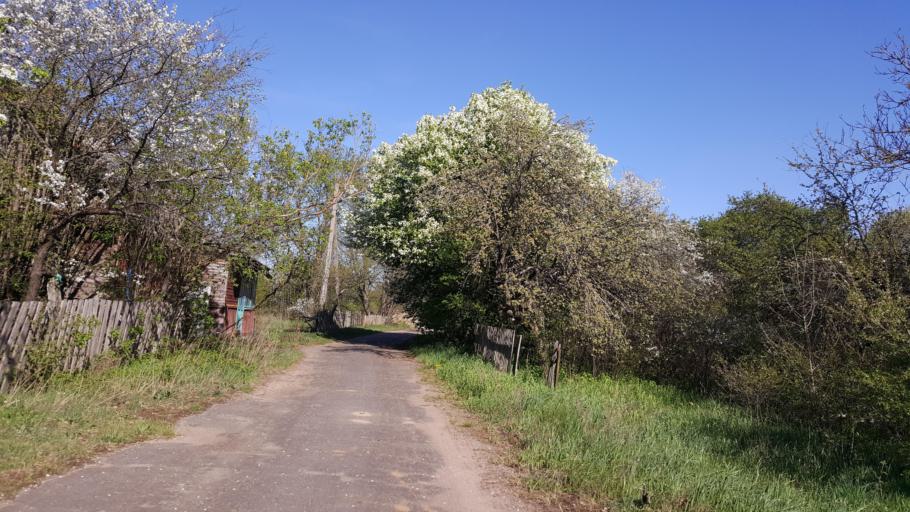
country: BY
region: Brest
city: Kamyanyets
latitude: 52.4411
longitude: 23.8822
